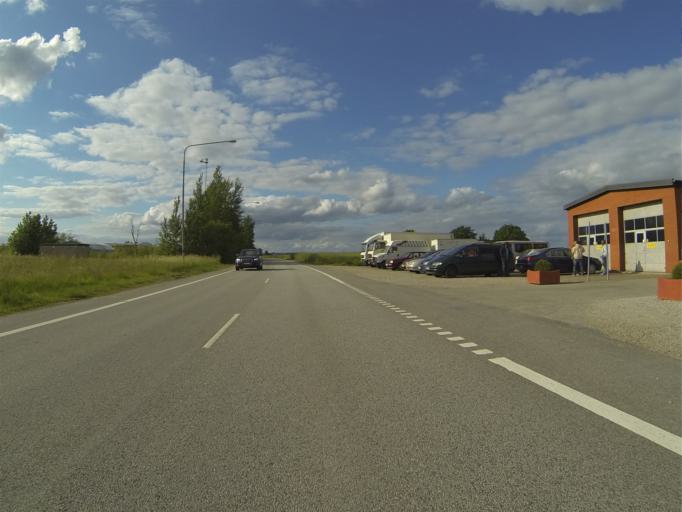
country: SE
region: Skane
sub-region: Staffanstorps Kommun
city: Staffanstorp
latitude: 55.6506
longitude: 13.2378
